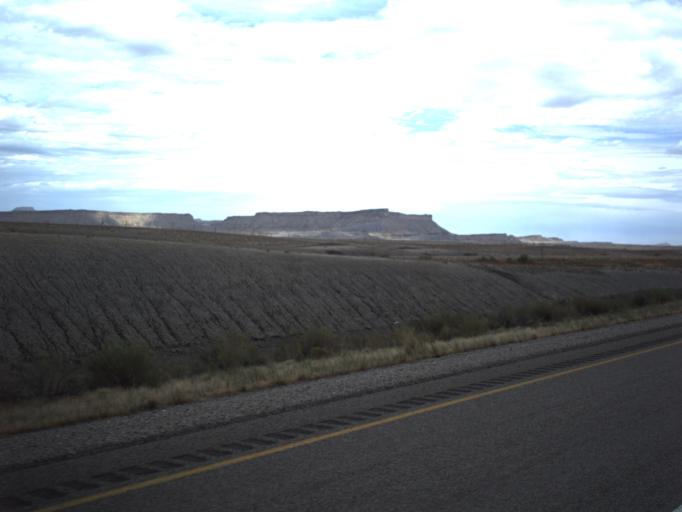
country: US
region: Utah
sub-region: Grand County
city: Moab
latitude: 38.9544
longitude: -110.0549
